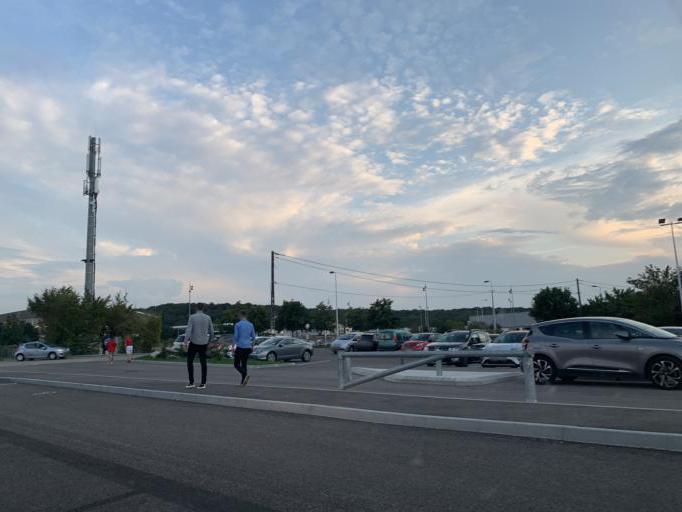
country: FR
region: Rhone-Alpes
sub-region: Departement de l'Ain
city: Bourg-en-Bresse
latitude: 46.1890
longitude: 5.2464
